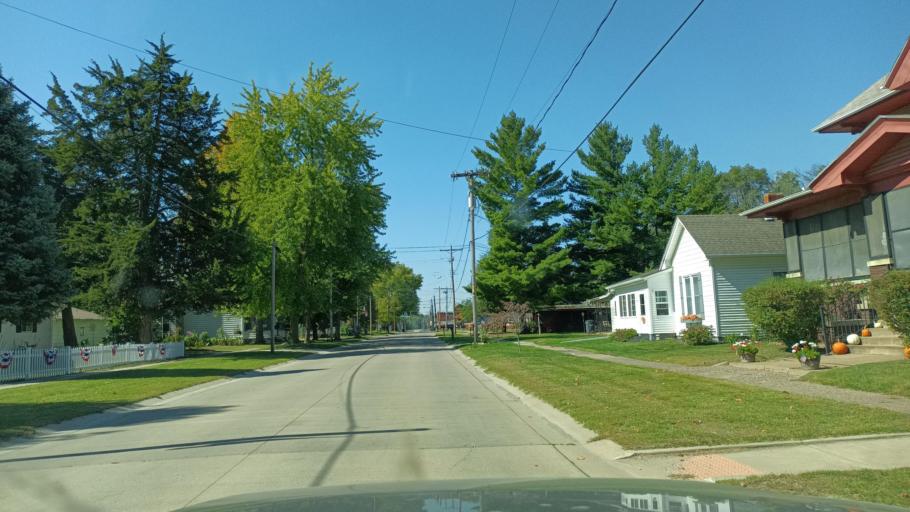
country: US
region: Illinois
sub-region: Henderson County
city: Oquawka
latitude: 41.1006
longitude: -90.9386
